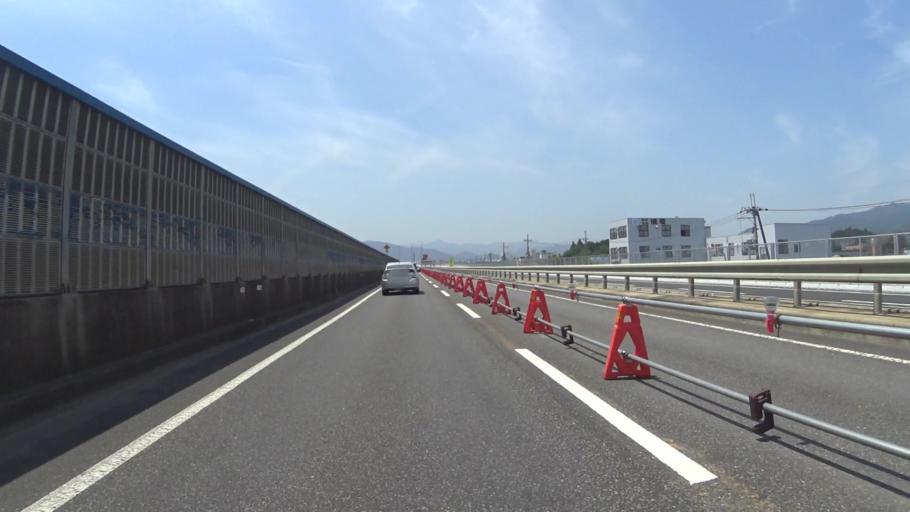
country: JP
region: Kyoto
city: Fukuchiyama
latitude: 35.2899
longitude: 135.1469
